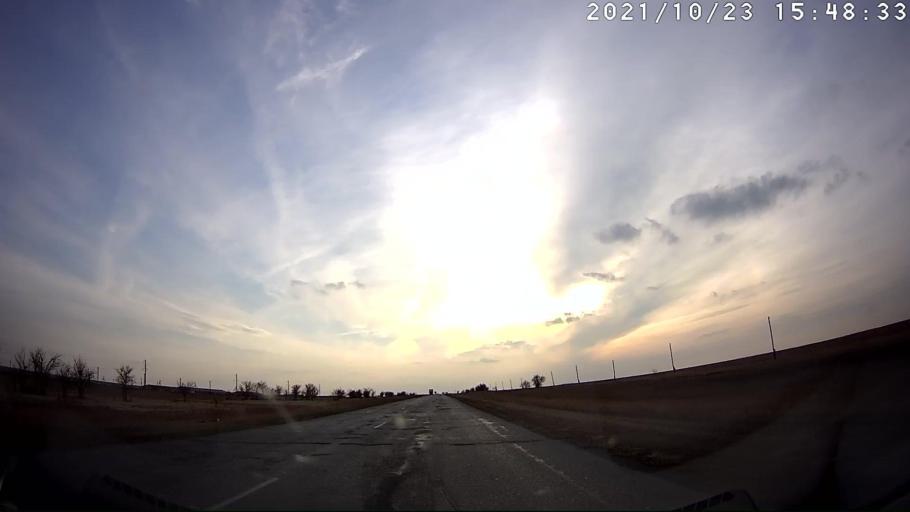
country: RU
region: Kalmykiya
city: Sadovoye
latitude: 48.0284
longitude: 44.0746
